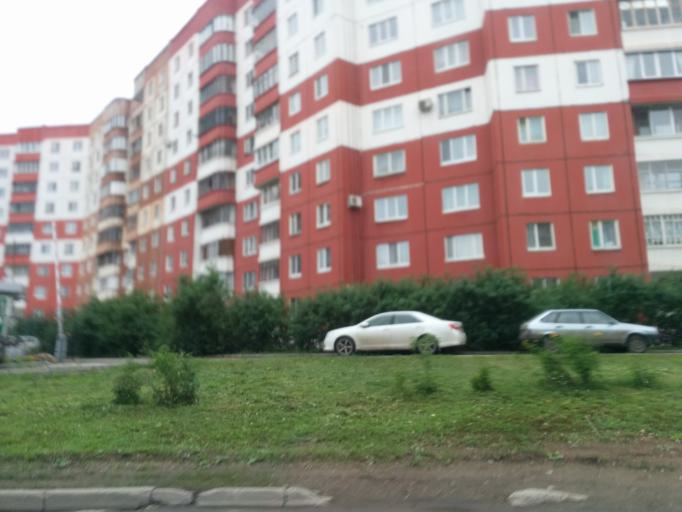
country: RU
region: Perm
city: Kondratovo
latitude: 57.9935
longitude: 56.1362
